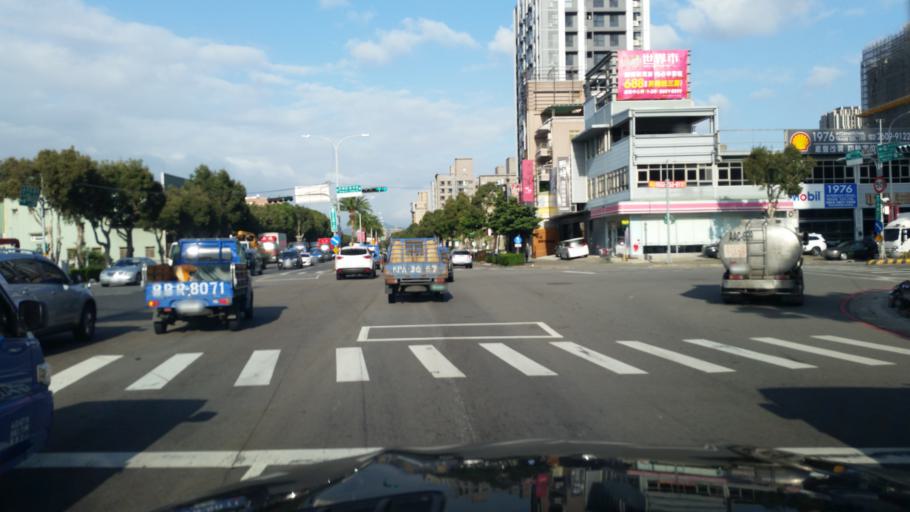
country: TW
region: Taiwan
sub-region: Taoyuan
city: Taoyuan
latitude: 25.0757
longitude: 121.3638
